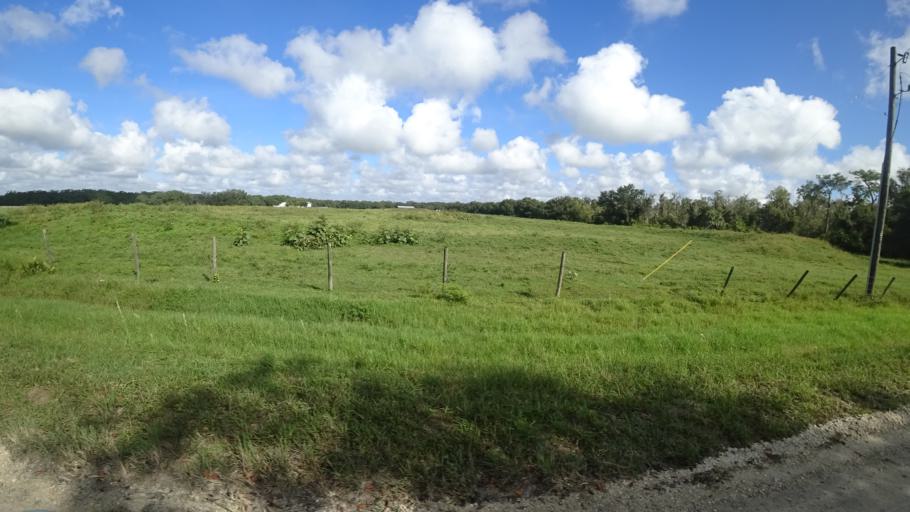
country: US
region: Florida
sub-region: Sarasota County
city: Lake Sarasota
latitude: 27.3249
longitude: -82.2120
